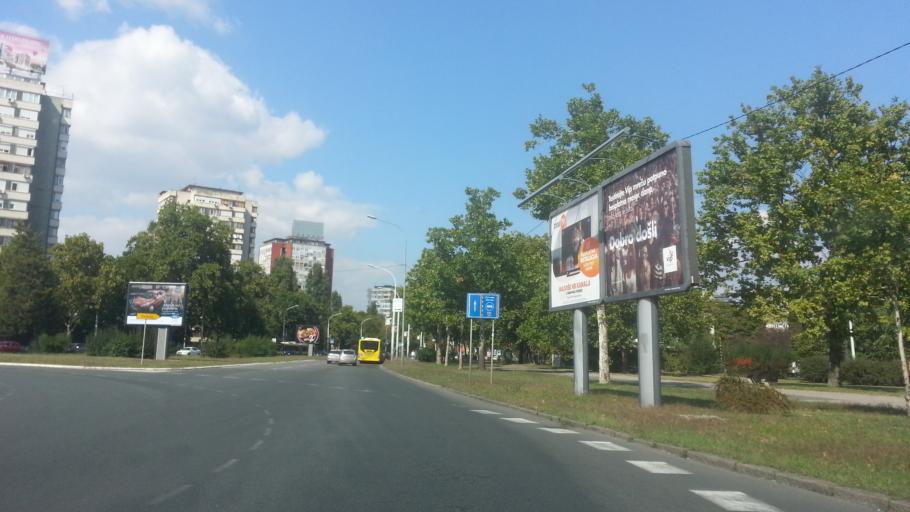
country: RS
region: Central Serbia
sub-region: Belgrade
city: Novi Beograd
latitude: 44.8244
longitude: 20.4138
